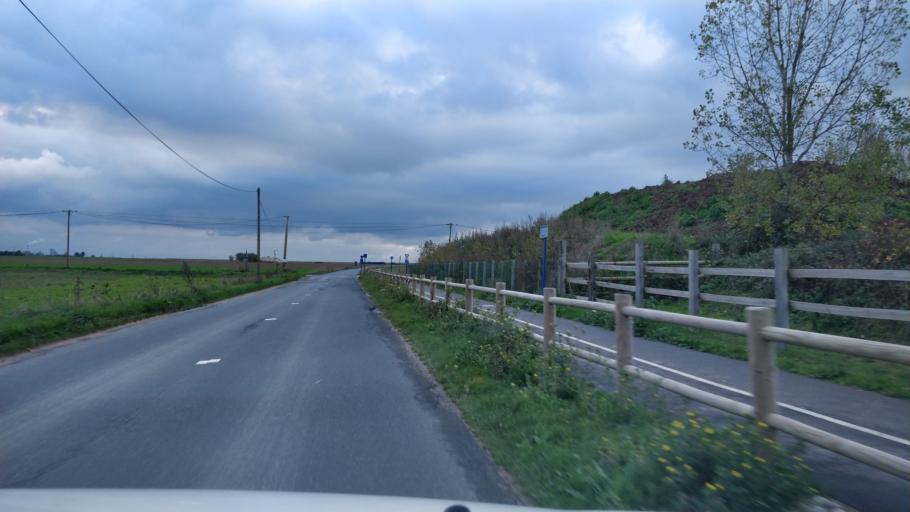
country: FR
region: Lower Normandy
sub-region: Departement du Calvados
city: Ouistreham
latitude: 49.2700
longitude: -0.2671
